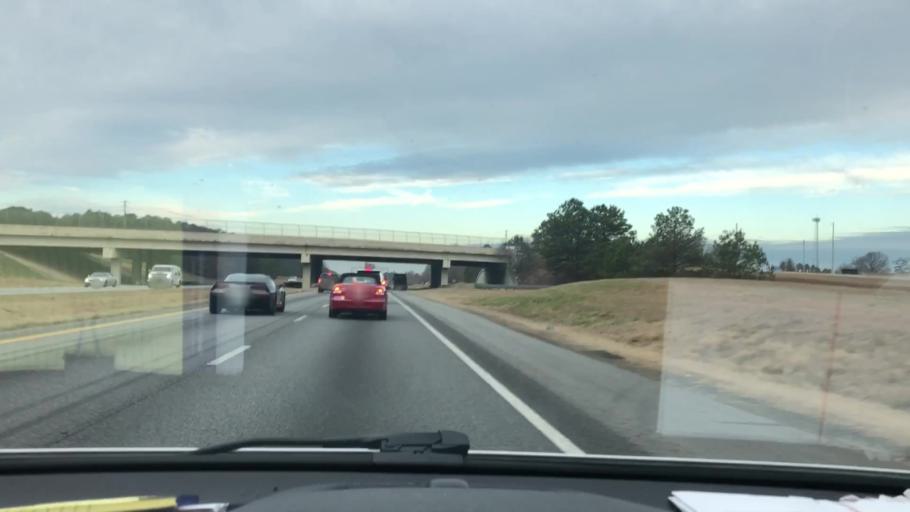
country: US
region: Georgia
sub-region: Gwinnett County
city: Lawrenceville
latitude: 33.9606
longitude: -84.0590
